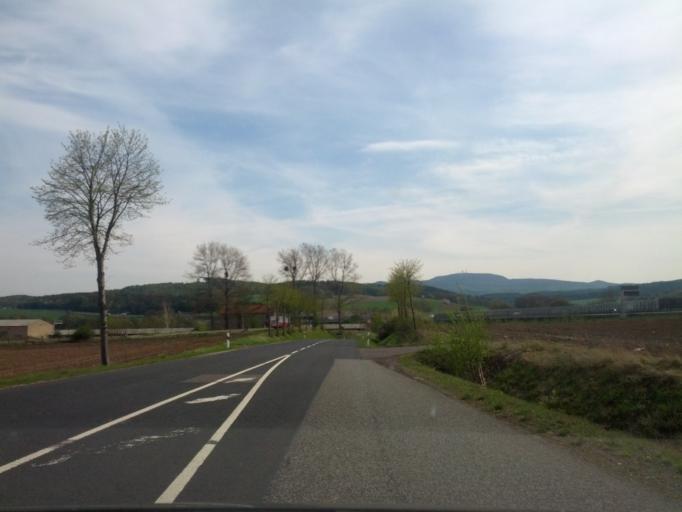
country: DE
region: Thuringia
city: Mechterstadt
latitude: 50.9493
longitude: 10.4881
